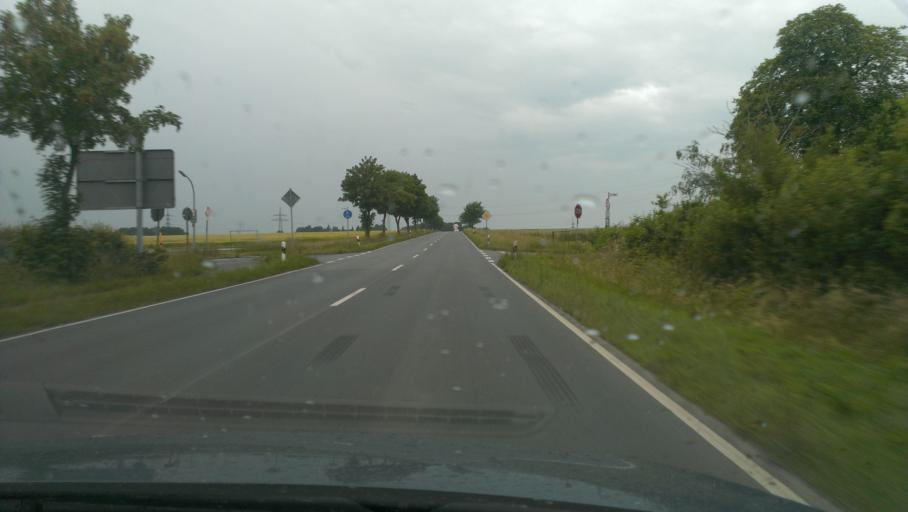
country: DE
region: North Rhine-Westphalia
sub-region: Regierungsbezirk Munster
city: Ennigerloh
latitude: 51.8067
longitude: 8.0232
